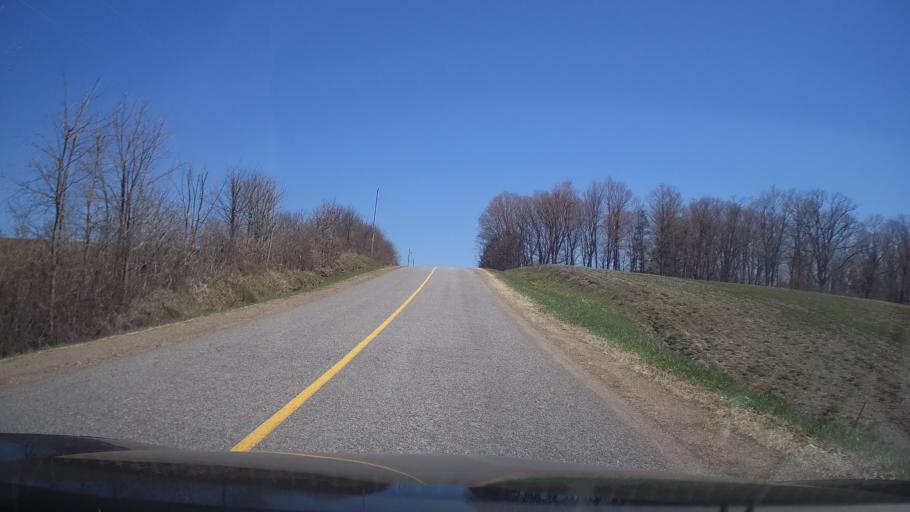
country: CA
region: Ontario
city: Arnprior
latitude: 45.5346
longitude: -76.3928
